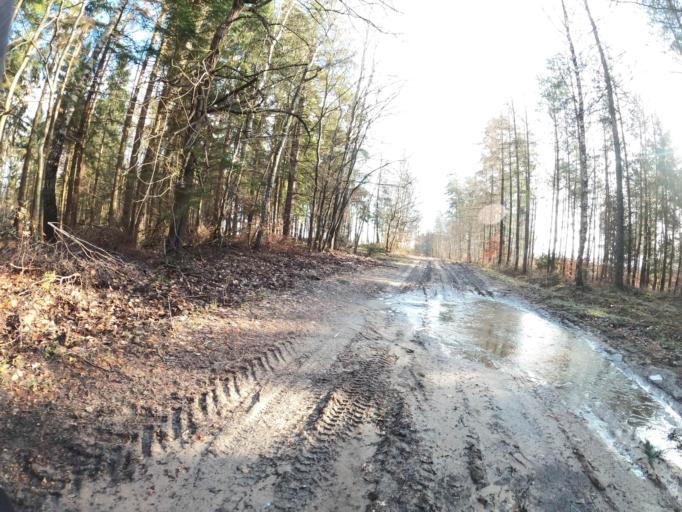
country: PL
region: West Pomeranian Voivodeship
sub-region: Powiat koszalinski
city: Polanow
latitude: 54.2100
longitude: 16.6474
